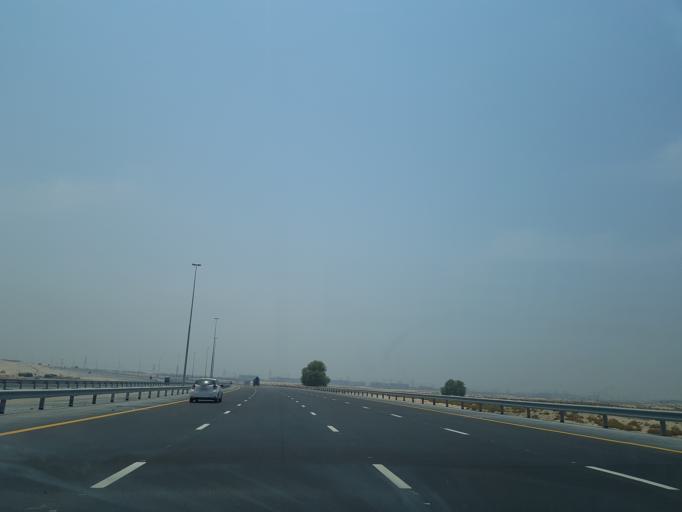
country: AE
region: Dubai
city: Dubai
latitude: 25.0093
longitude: 55.1975
